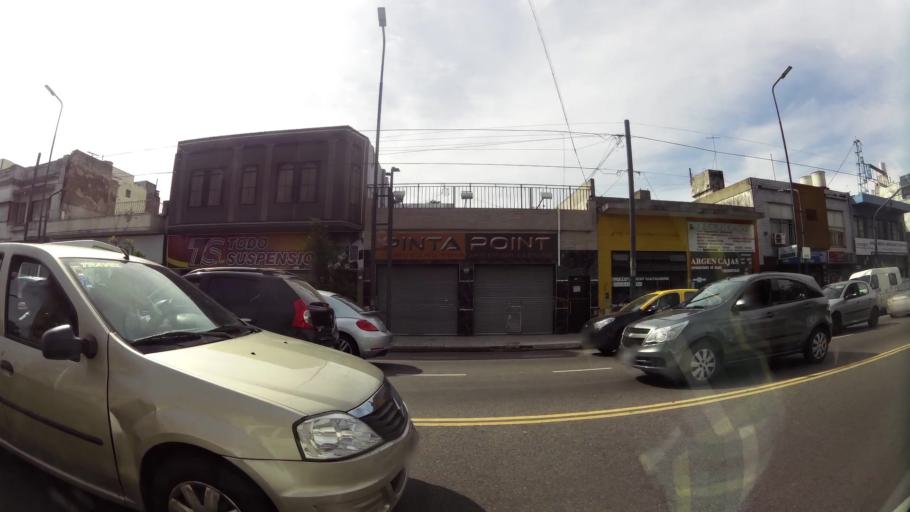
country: AR
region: Buenos Aires
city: San Justo
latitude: -34.6613
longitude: -58.5163
